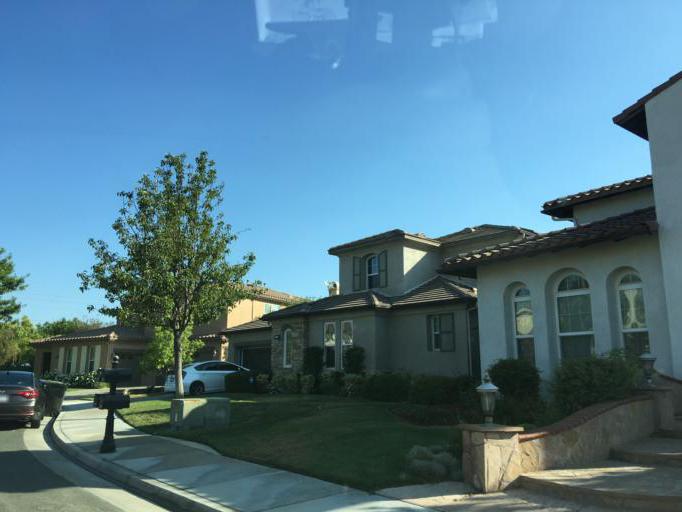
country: US
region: California
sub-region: Los Angeles County
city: Valencia
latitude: 34.4093
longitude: -118.5921
